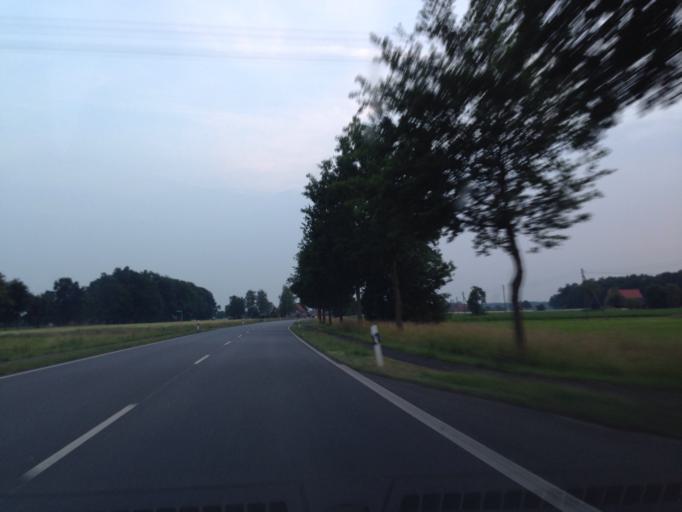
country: DE
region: North Rhine-Westphalia
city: Ludinghausen
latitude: 51.7932
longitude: 7.4694
